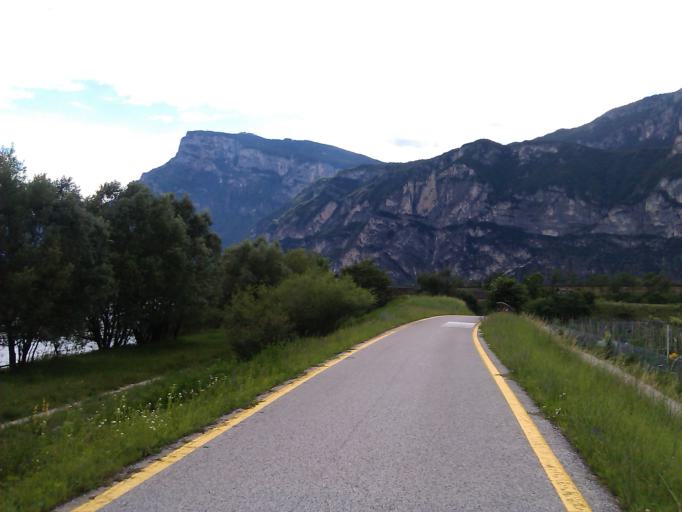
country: IT
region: Trentino-Alto Adige
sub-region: Provincia di Trento
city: San Michele All'Adige
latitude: 46.1914
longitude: 11.1247
